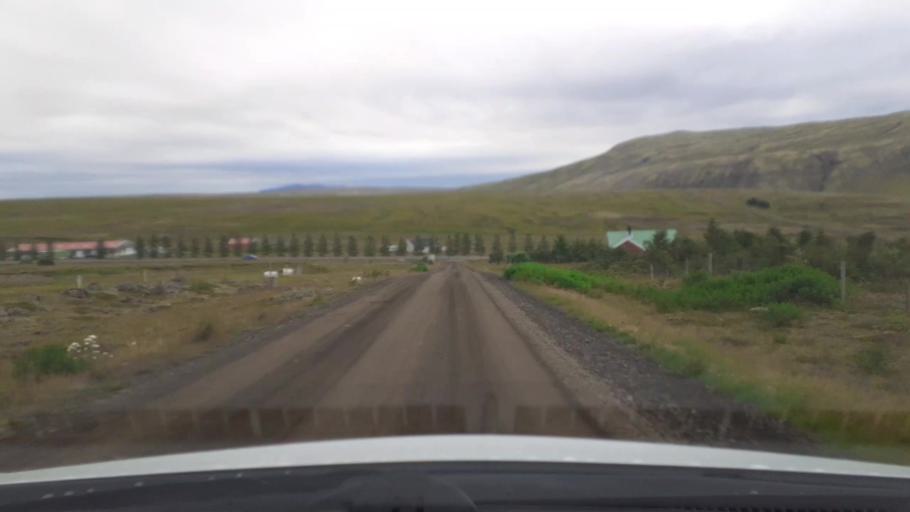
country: IS
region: Capital Region
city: Mosfellsbaer
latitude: 64.1908
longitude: -21.5391
